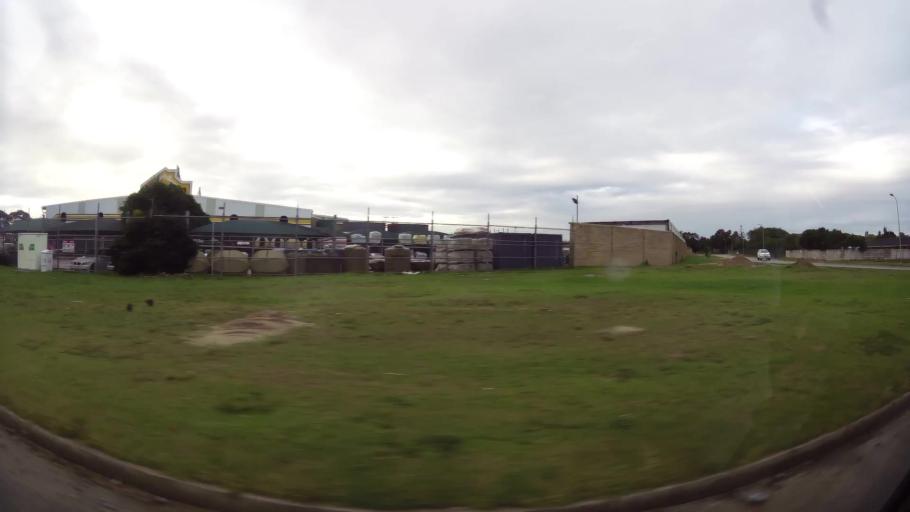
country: ZA
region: Eastern Cape
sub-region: Nelson Mandela Bay Metropolitan Municipality
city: Port Elizabeth
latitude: -33.9926
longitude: 25.5519
